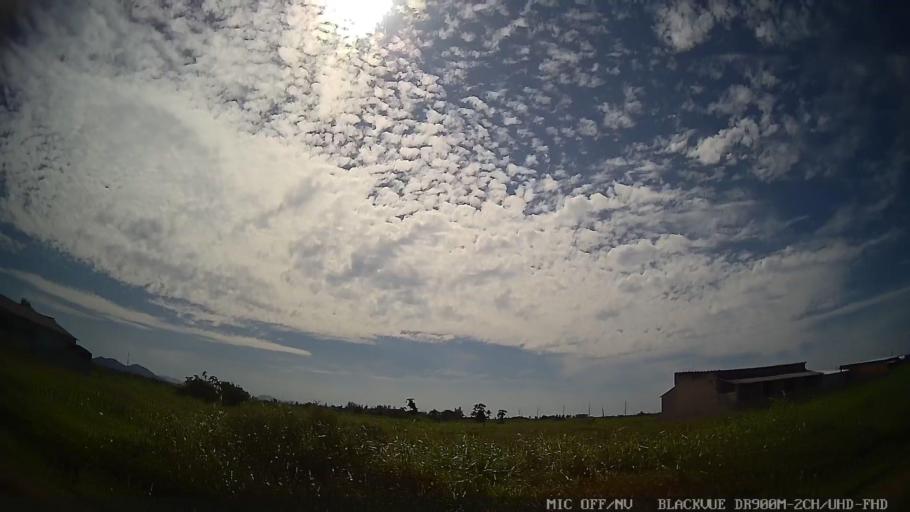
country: BR
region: Sao Paulo
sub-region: Iguape
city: Iguape
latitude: -24.7793
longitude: -47.6025
